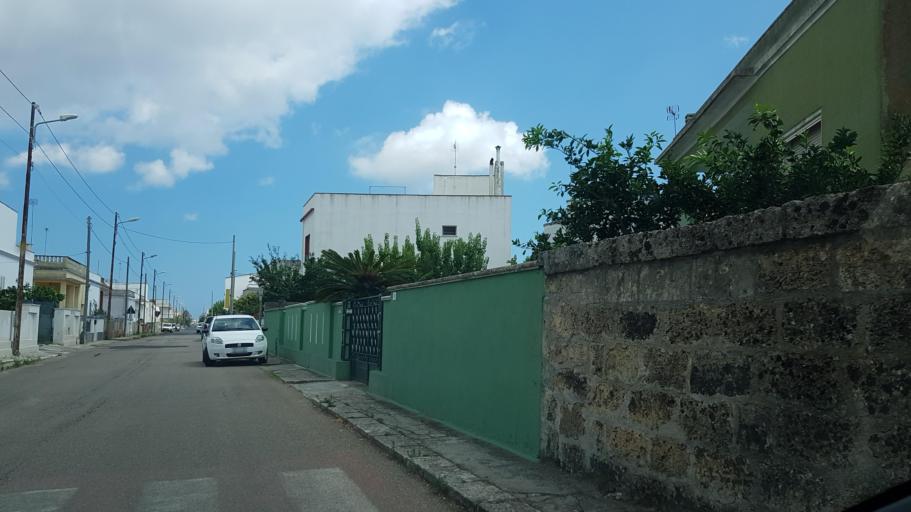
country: IT
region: Apulia
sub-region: Provincia di Lecce
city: Patu
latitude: 39.8427
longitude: 18.3382
